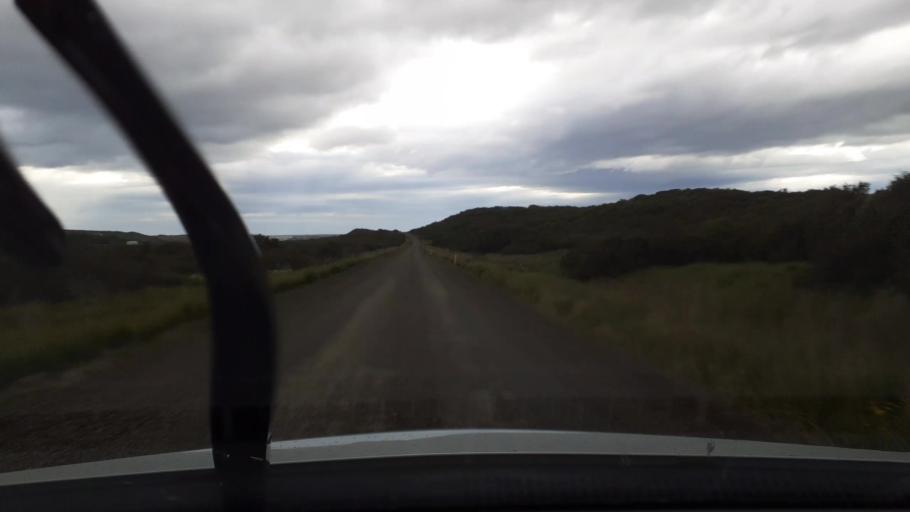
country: IS
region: West
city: Borgarnes
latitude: 64.6010
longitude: -21.9733
